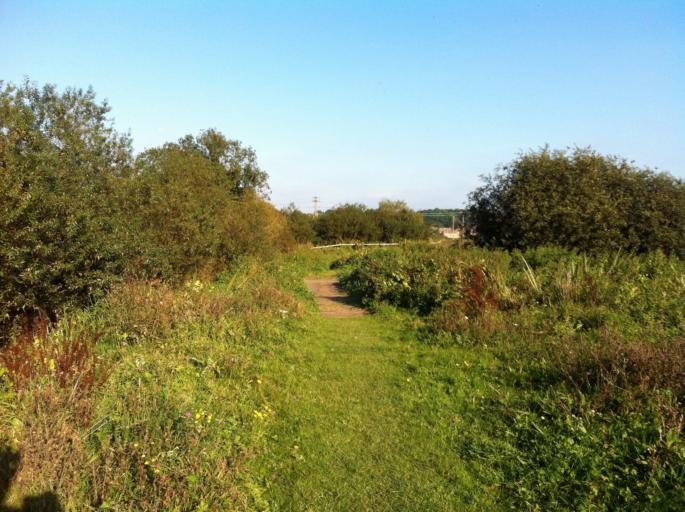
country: GB
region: England
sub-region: Norfolk
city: Bowthorpe
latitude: 52.6320
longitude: 1.2239
